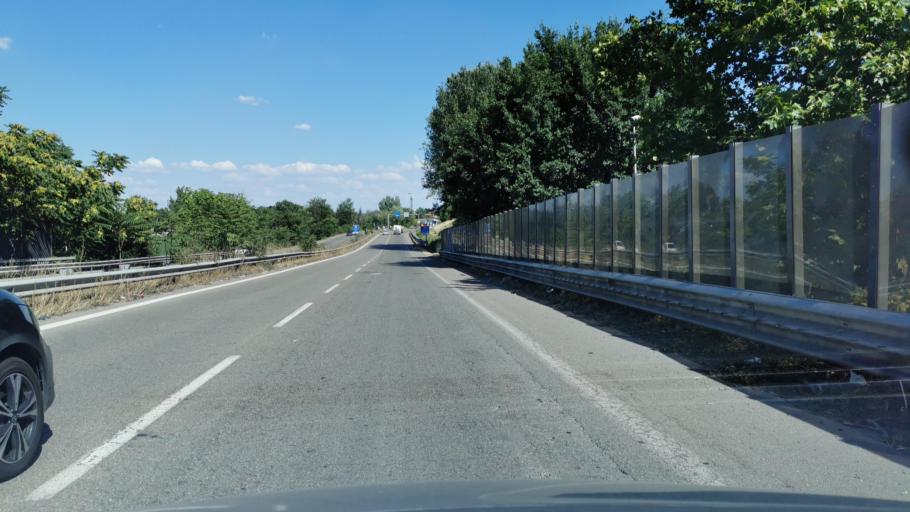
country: IT
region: Emilia-Romagna
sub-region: Provincia di Modena
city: Modena
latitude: 44.6599
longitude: 10.9476
